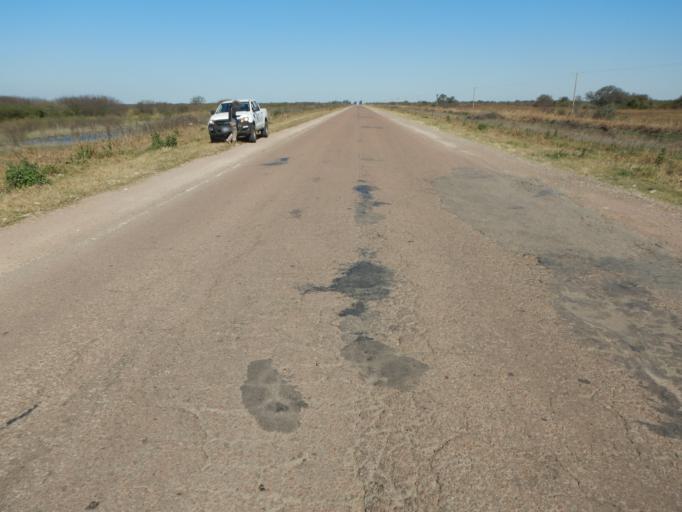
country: AR
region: Santiago del Estero
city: Los Juries
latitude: -28.6453
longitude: -61.5257
